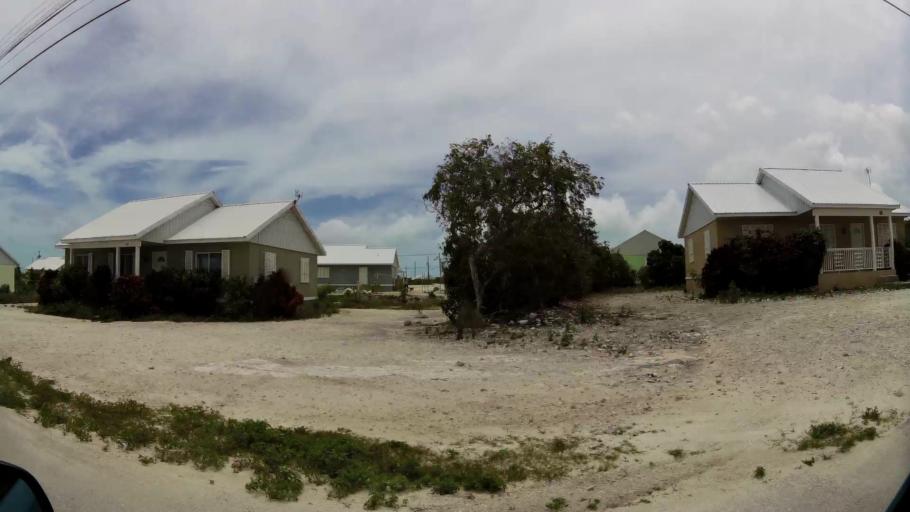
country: BS
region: Mayaguana
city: Abraham's Bay
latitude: 21.8070
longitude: -72.2978
